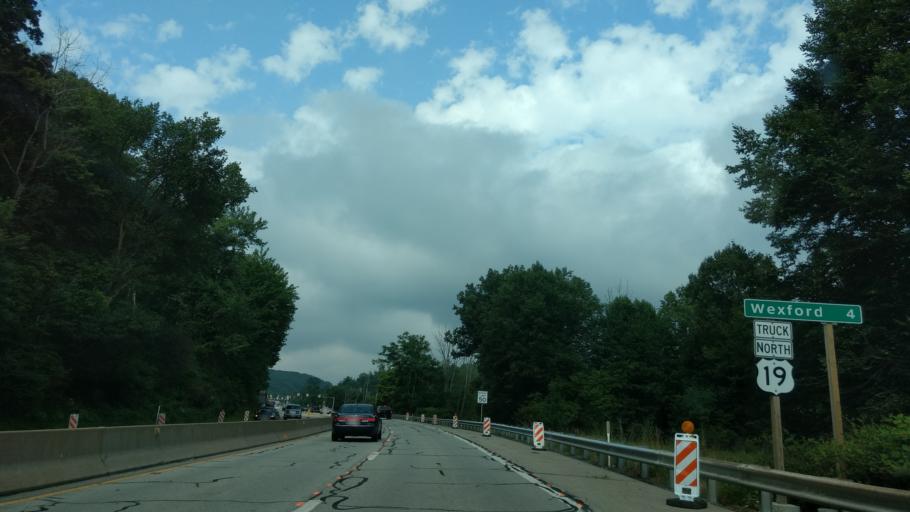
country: US
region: Pennsylvania
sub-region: Allegheny County
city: Franklin Park
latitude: 40.5848
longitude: -80.0327
